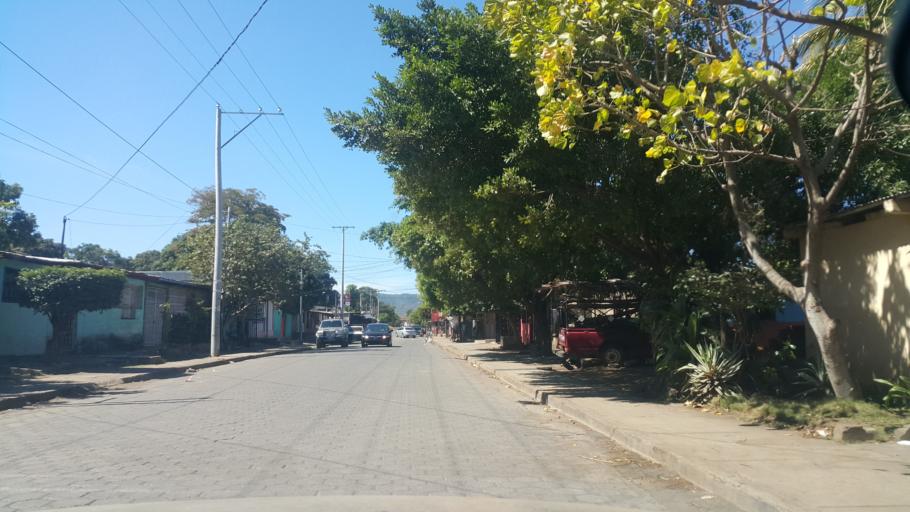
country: NI
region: Managua
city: Ciudad Sandino
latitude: 12.1478
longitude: -86.3471
